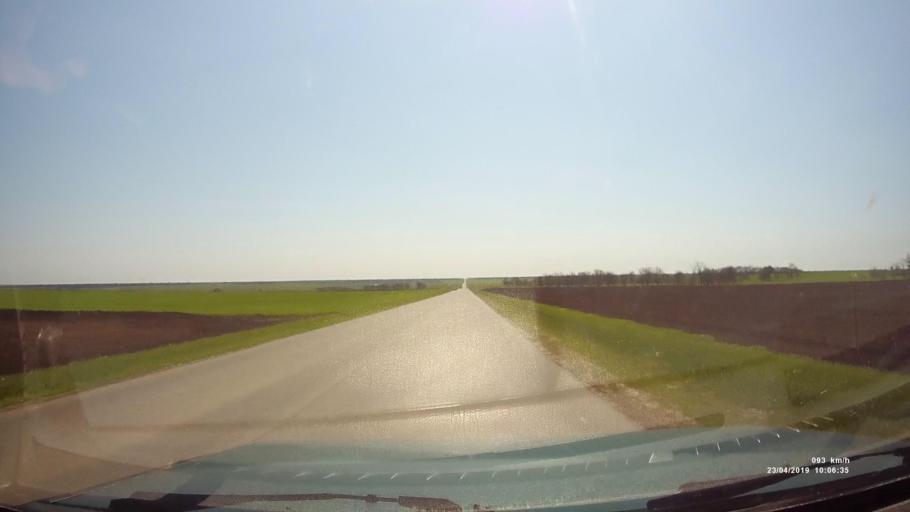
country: RU
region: Rostov
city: Sovetskoye
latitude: 46.7316
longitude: 42.2397
